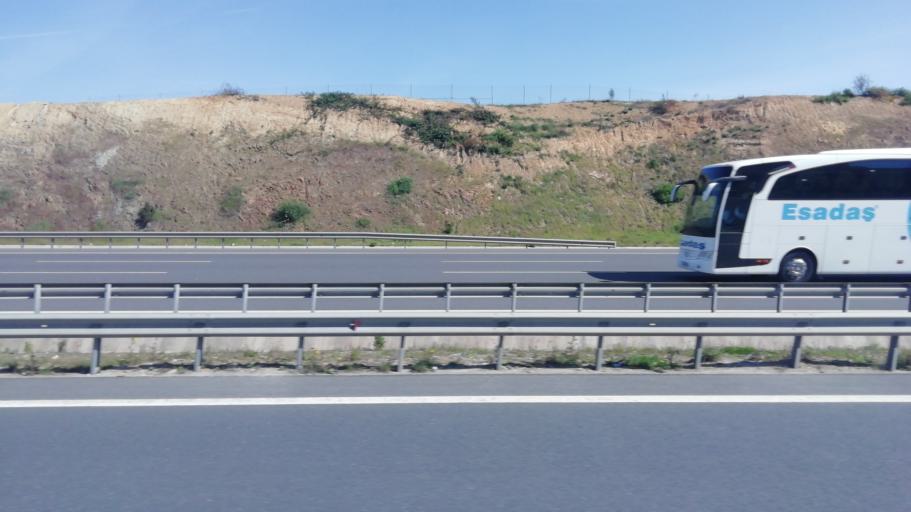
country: TR
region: Istanbul
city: Arikoey
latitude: 41.2333
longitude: 28.9604
